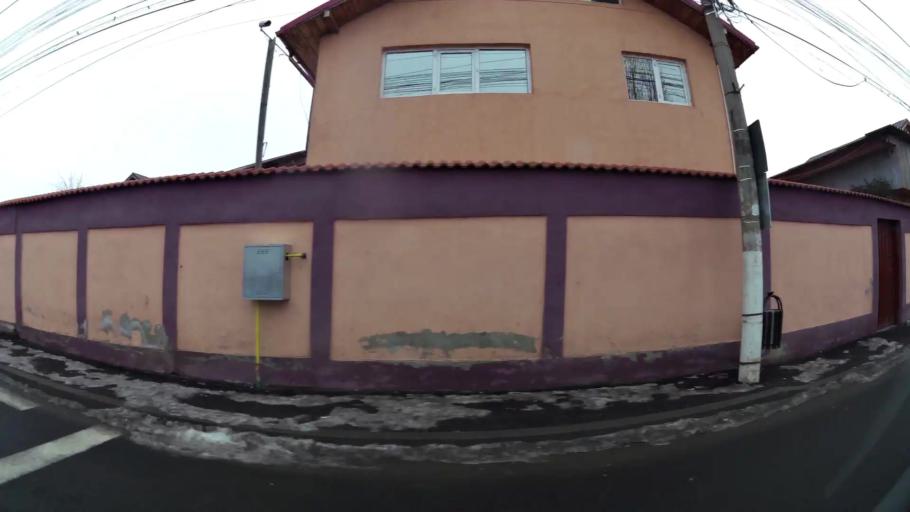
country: RO
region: Ilfov
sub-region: Comuna Pantelimon
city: Pantelimon
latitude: 44.4599
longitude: 26.2105
